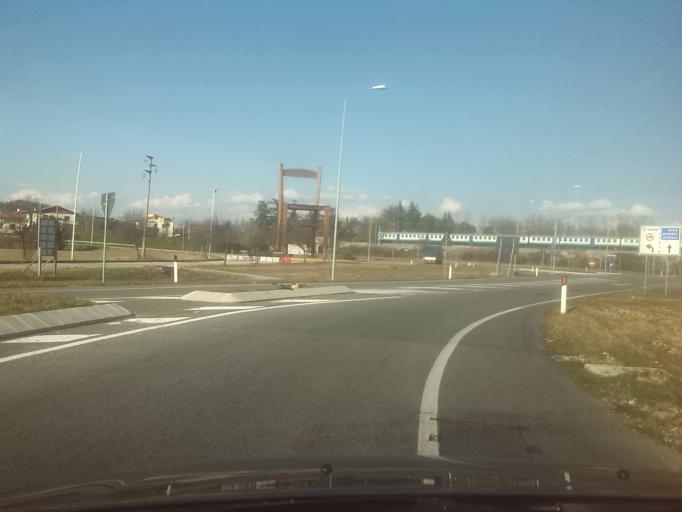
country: IT
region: Friuli Venezia Giulia
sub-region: Provincia di Udine
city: Manzano
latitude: 45.9825
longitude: 13.3812
